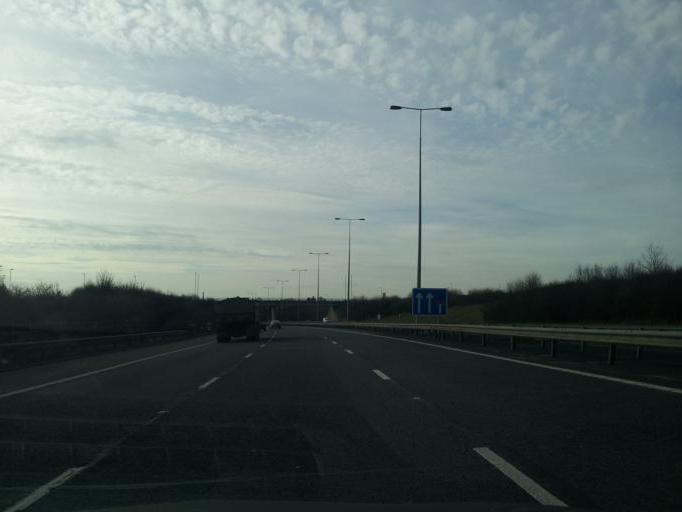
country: GB
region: England
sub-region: Cambridgeshire
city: Great Stukeley
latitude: 52.3639
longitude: -0.2552
